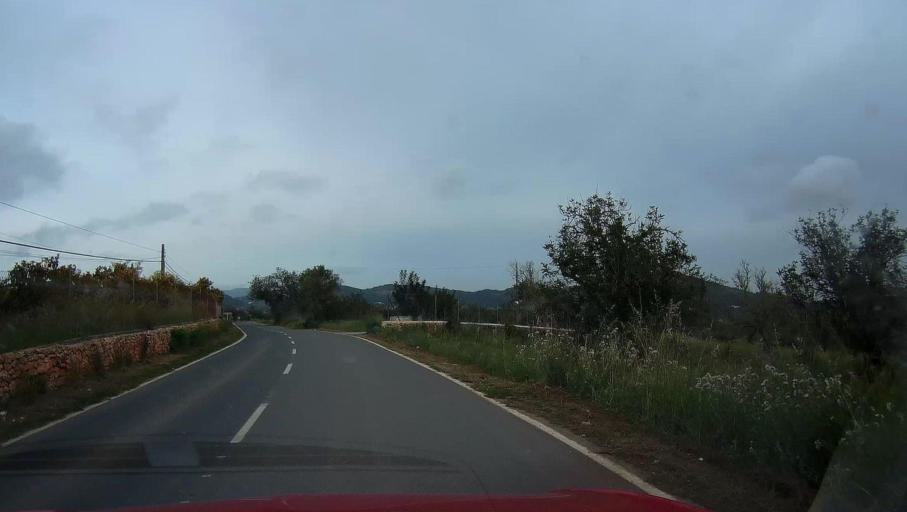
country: ES
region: Balearic Islands
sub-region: Illes Balears
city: Sant Joan de Labritja
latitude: 39.0490
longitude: 1.4239
